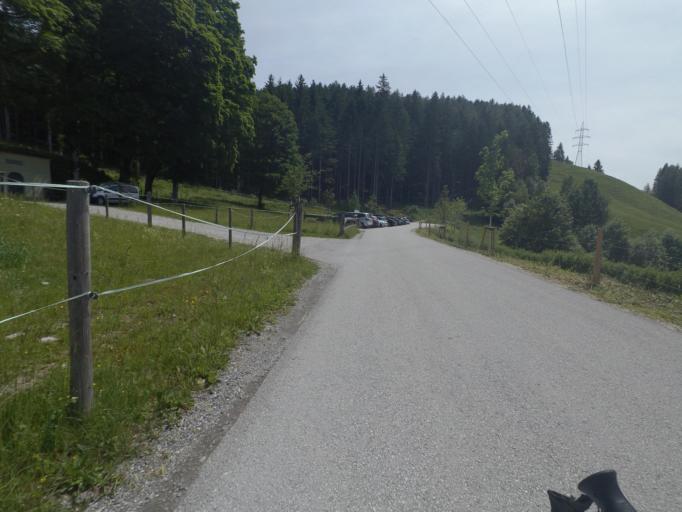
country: AT
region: Salzburg
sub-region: Politischer Bezirk Zell am See
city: Saalfelden am Steinernen Meer
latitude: 47.4389
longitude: 12.8614
